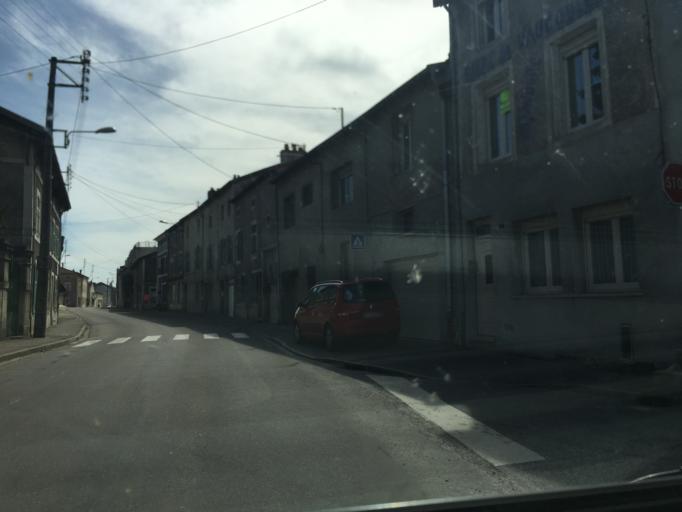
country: FR
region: Lorraine
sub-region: Departement de la Meuse
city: Lerouville
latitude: 48.7913
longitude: 5.5439
